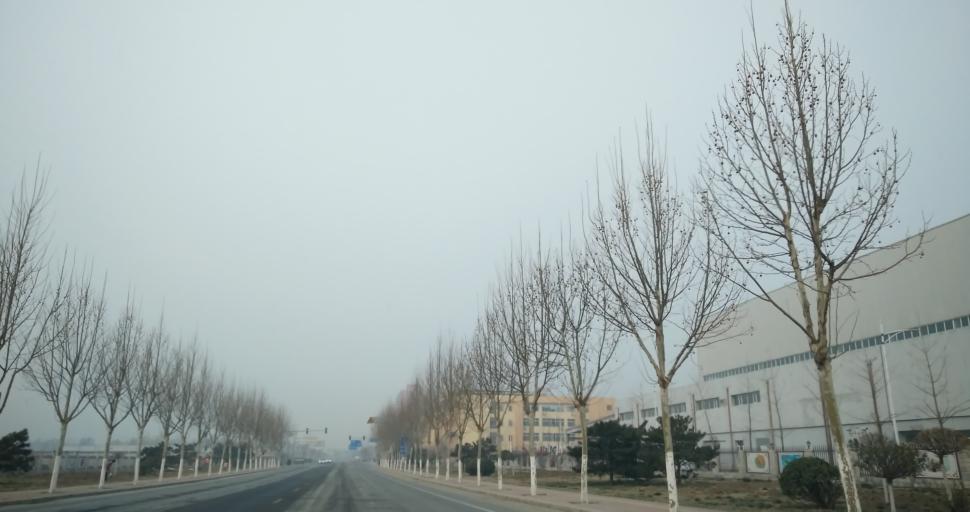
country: CN
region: Beijing
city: Yinghai
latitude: 39.7532
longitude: 116.4376
